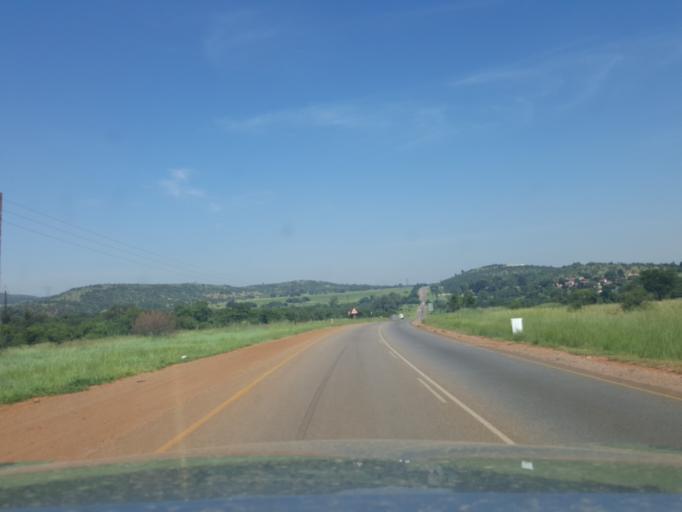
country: ZA
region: Gauteng
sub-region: City of Tshwane Metropolitan Municipality
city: Cullinan
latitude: -25.6805
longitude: 28.3689
